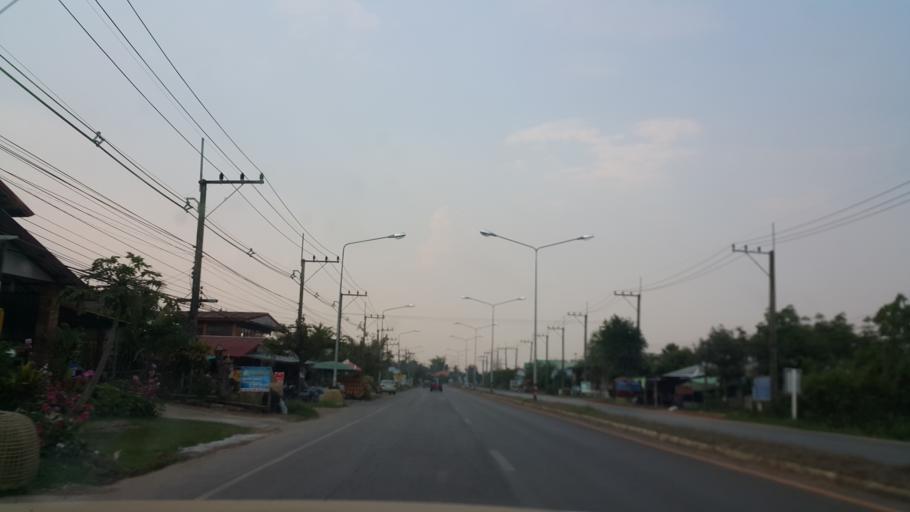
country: TH
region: Nakhon Phanom
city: That Phanom
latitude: 16.9894
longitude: 104.7256
